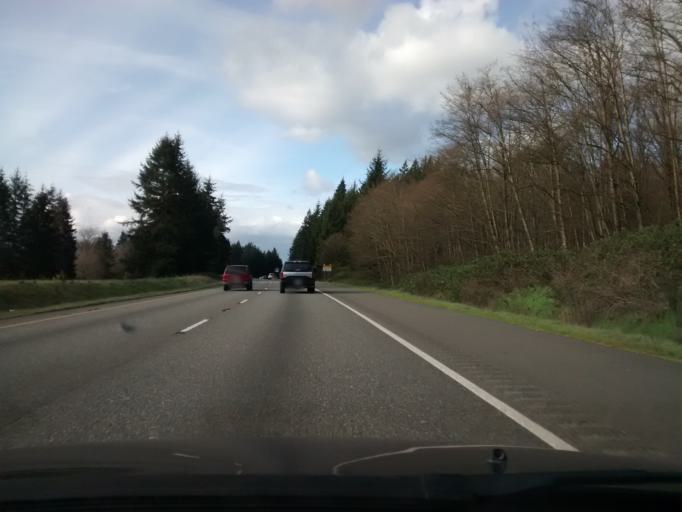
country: US
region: Washington
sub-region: Kitsap County
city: Burley
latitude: 47.4197
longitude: -122.6227
